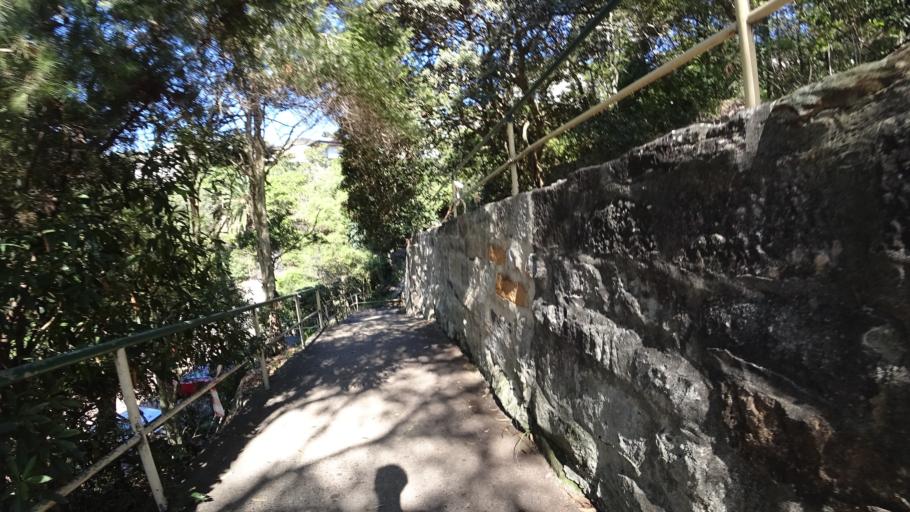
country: AU
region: New South Wales
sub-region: Mosman
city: Mosman
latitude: -33.8392
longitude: 151.2517
